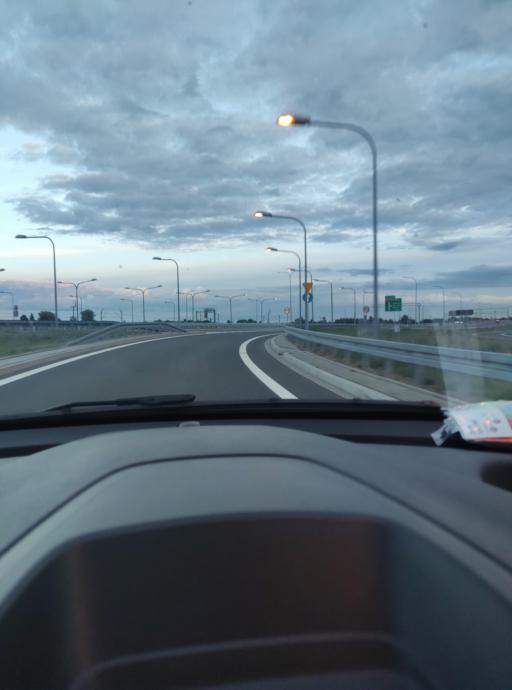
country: PL
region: Masovian Voivodeship
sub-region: Powiat piaseczynski
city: Mysiadlo
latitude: 52.1355
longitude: 20.9877
